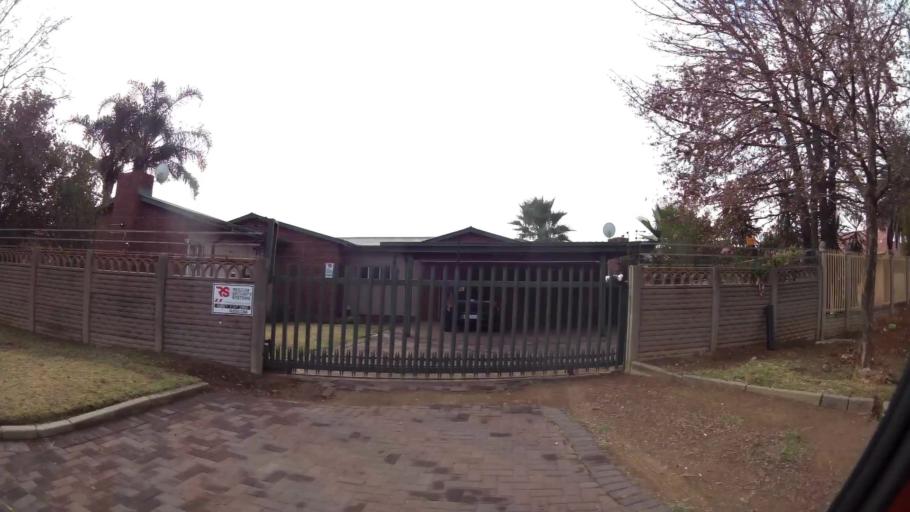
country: ZA
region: Gauteng
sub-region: Sedibeng District Municipality
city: Vanderbijlpark
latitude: -26.6920
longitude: 27.8492
